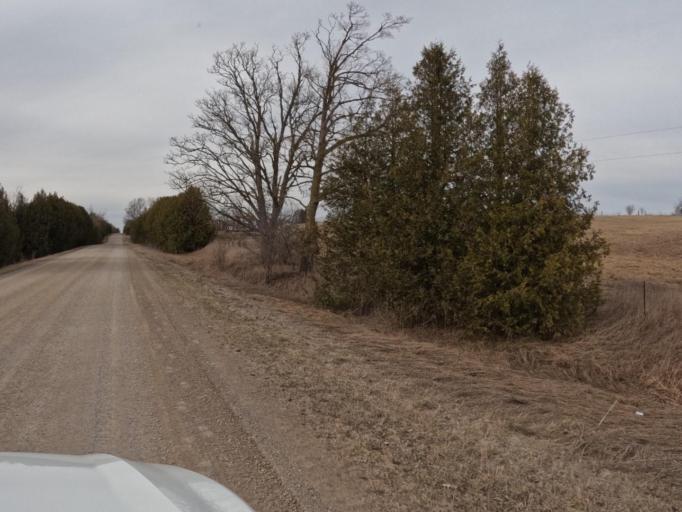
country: CA
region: Ontario
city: Orangeville
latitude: 43.9223
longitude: -80.2559
